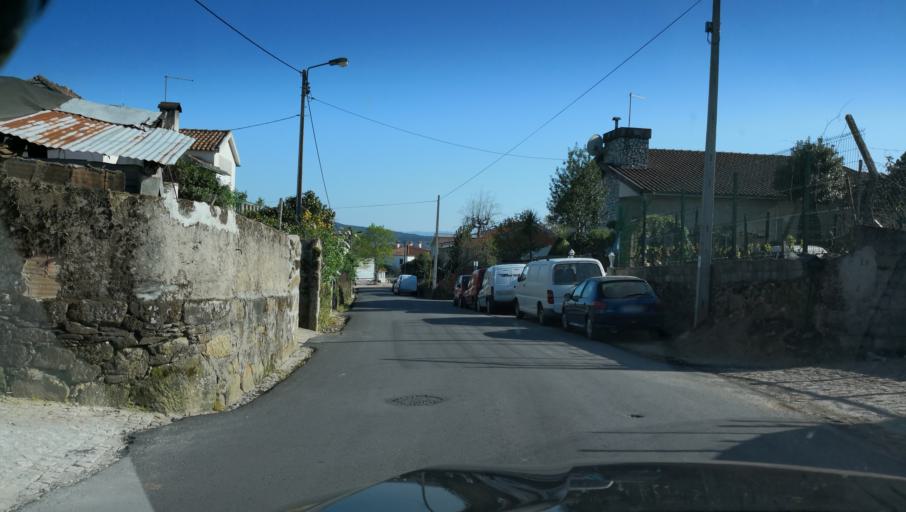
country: PT
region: Vila Real
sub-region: Vila Real
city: Vila Real
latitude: 41.2821
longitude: -7.6840
